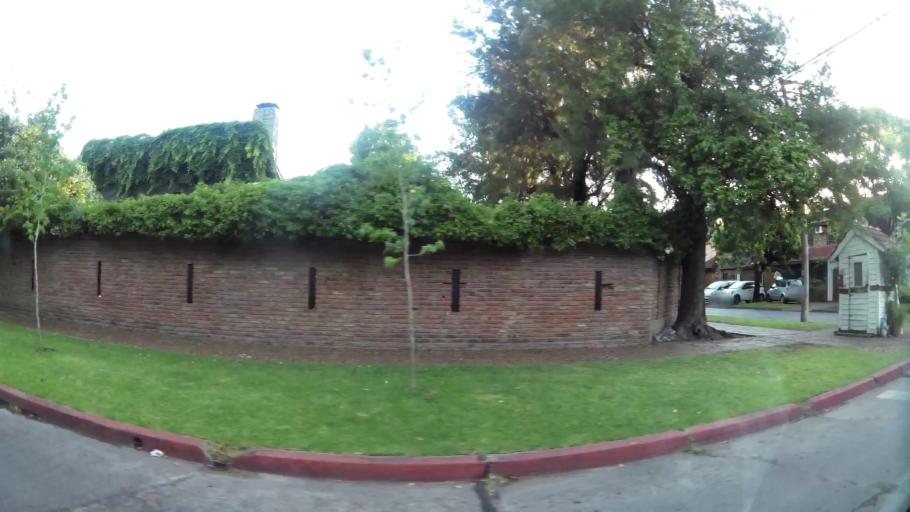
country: AR
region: Buenos Aires
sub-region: Partido de Moron
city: Moron
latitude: -34.6483
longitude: -58.6358
